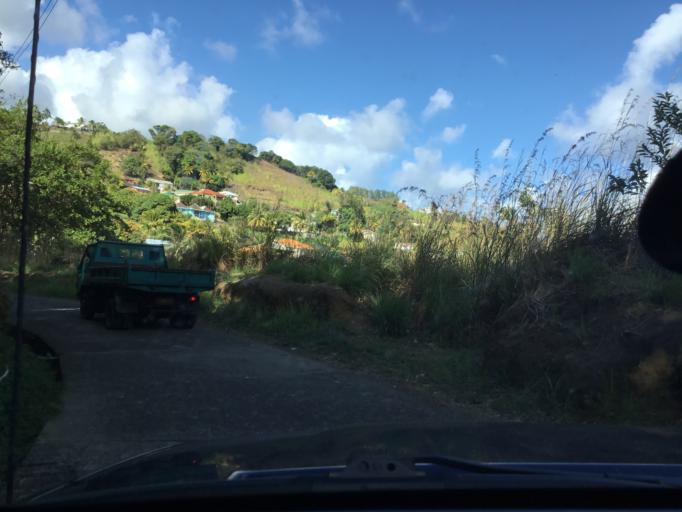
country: VC
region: Charlotte
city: Biabou
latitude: 13.1590
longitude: -61.1685
